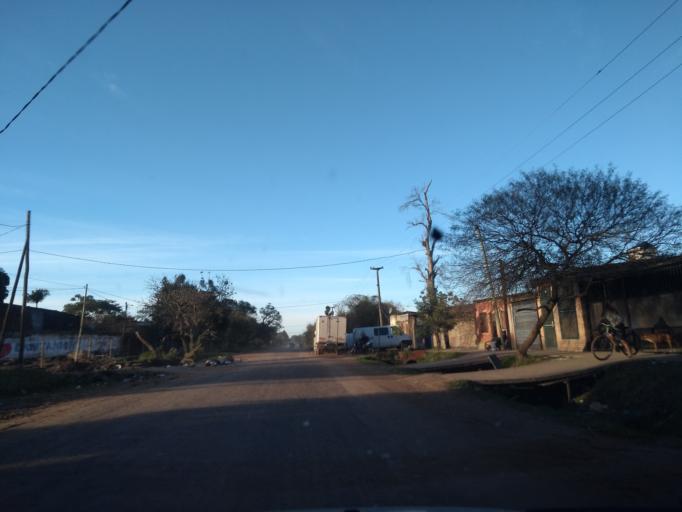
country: AR
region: Chaco
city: Resistencia
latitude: -27.4885
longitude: -58.9710
